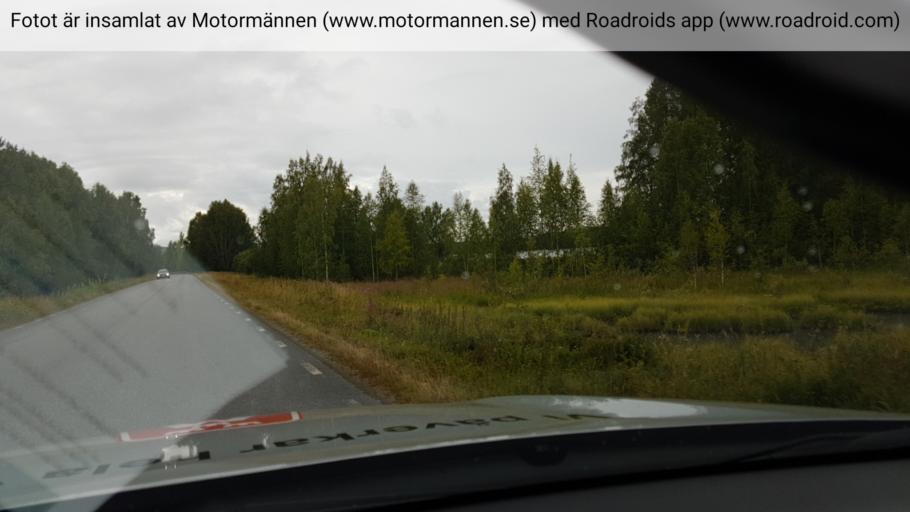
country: SE
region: Norrbotten
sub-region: Bodens Kommun
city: Boden
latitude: 65.8260
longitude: 21.5524
